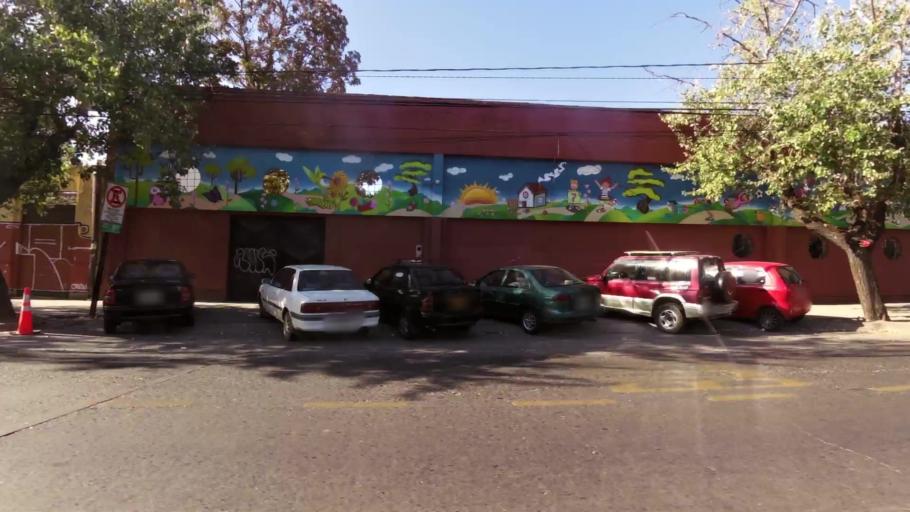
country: CL
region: Maule
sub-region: Provincia de Talca
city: Talca
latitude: -35.4294
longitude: -71.6516
